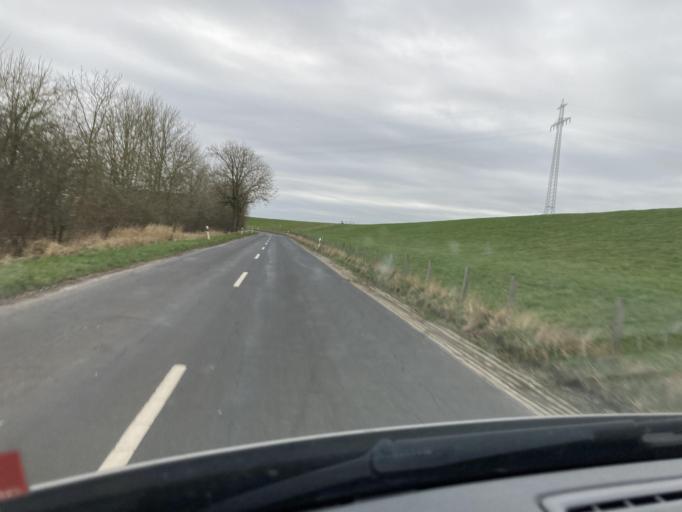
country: DE
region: Lower Saxony
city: Leer
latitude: 53.2120
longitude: 7.4379
